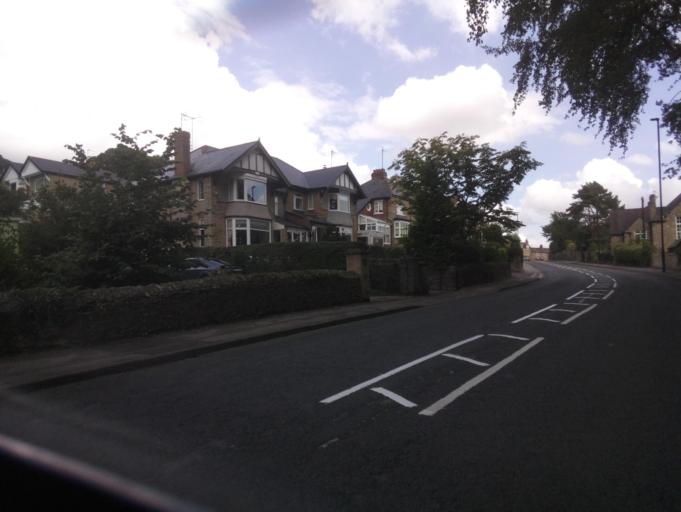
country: GB
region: England
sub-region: North Yorkshire
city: Catterick Garrison
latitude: 54.4050
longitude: -1.7479
